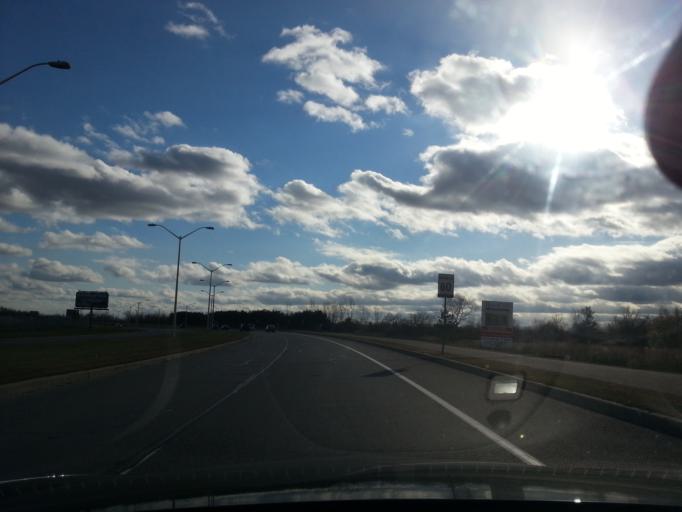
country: CA
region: Ontario
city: Ottawa
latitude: 45.3311
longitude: -75.6940
